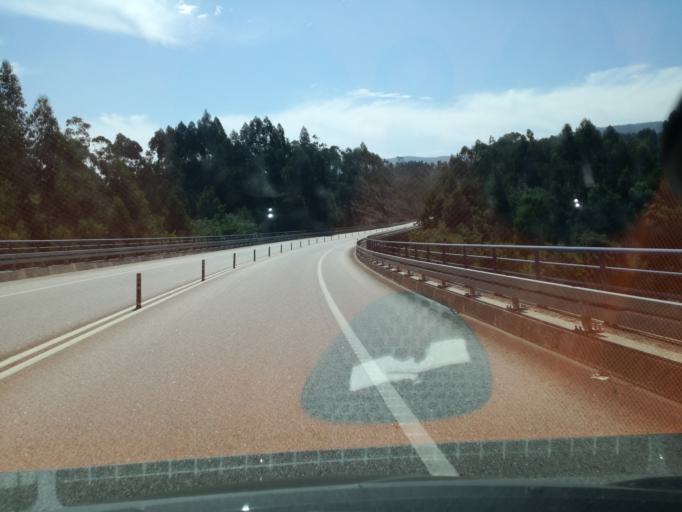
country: PT
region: Viana do Castelo
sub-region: Vila Nova de Cerveira
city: Vila Nova de Cerveira
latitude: 41.8961
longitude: -8.7741
